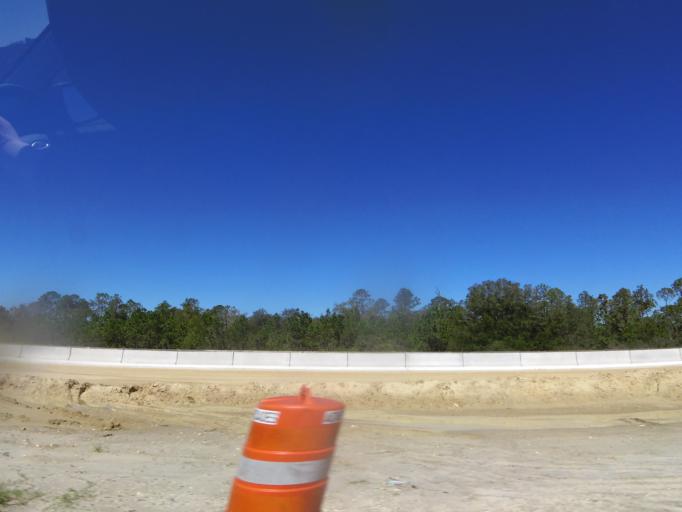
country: US
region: Florida
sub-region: Seminole County
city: Heathrow
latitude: 28.8150
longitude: -81.4298
